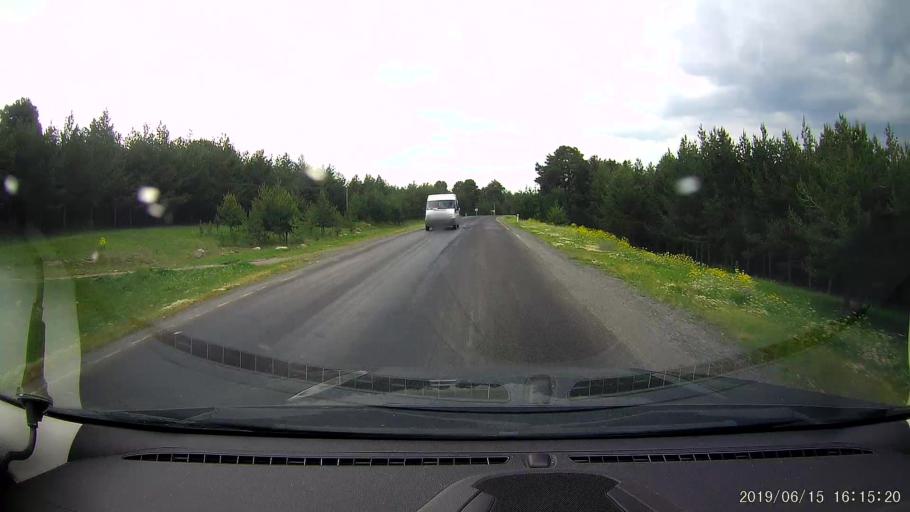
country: TR
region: Ardahan
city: Hanak
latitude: 41.2696
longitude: 42.8554
